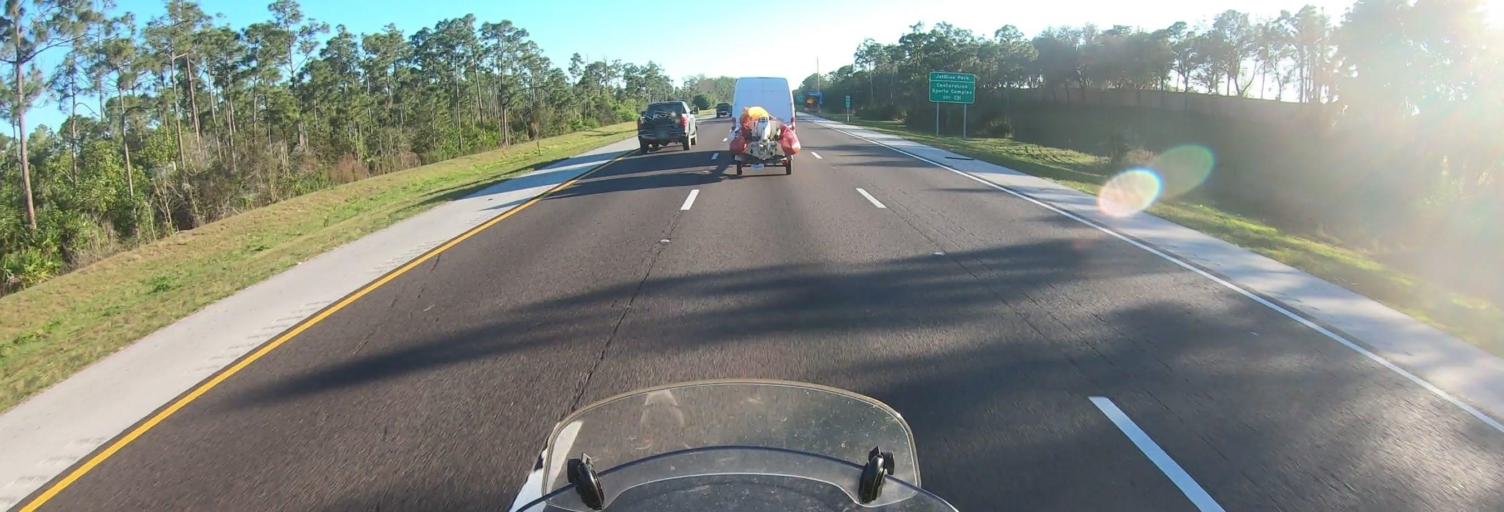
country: US
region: Florida
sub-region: Lee County
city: Gateway
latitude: 26.5652
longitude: -81.7953
